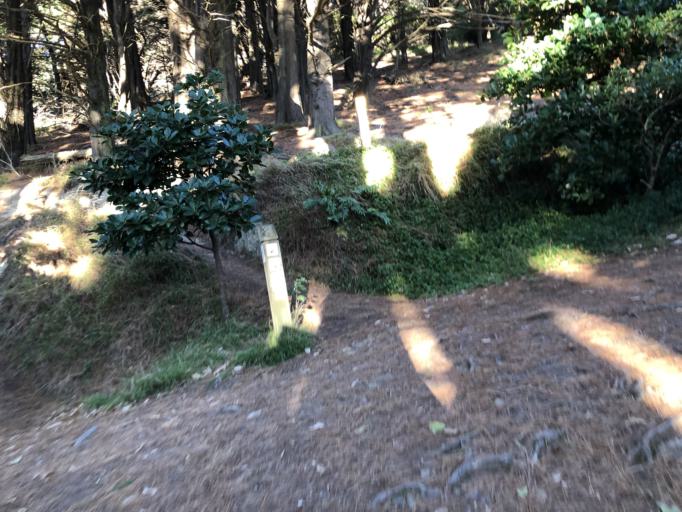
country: NZ
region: Wellington
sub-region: Wellington City
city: Wellington
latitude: -41.3001
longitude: 174.7886
